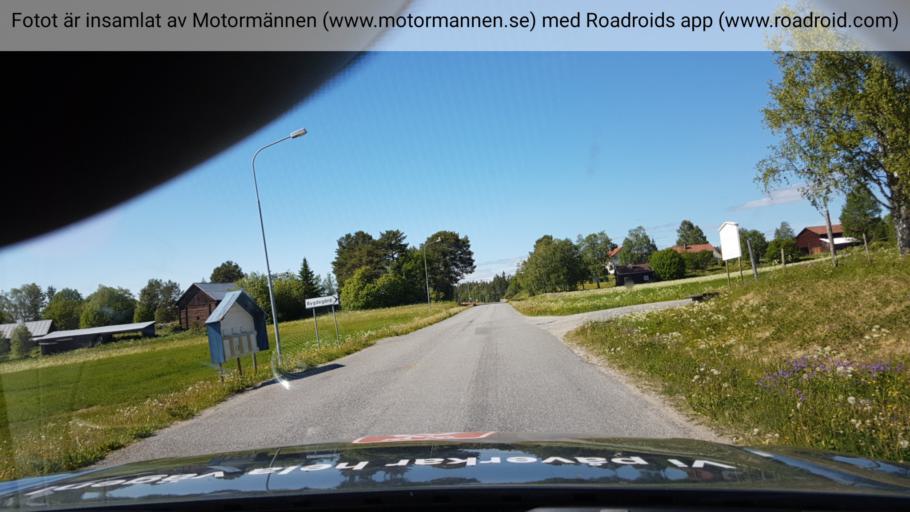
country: SE
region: Jaemtland
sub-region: OEstersunds Kommun
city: Brunflo
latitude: 62.9930
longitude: 14.8803
